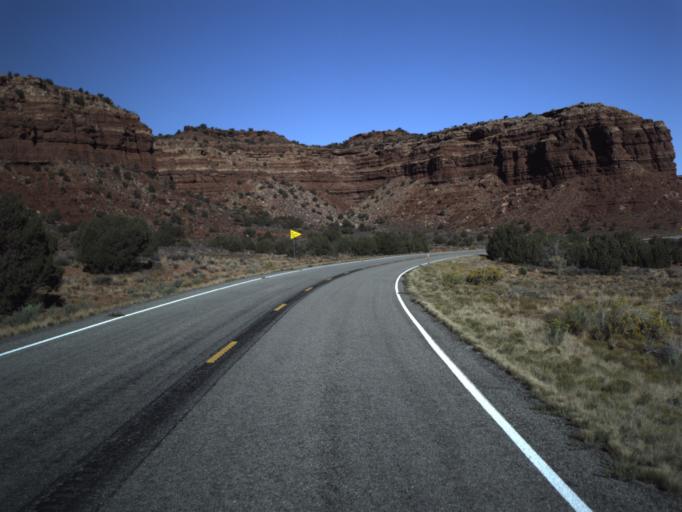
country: US
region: Utah
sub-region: San Juan County
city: Blanding
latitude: 37.7055
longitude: -110.2402
